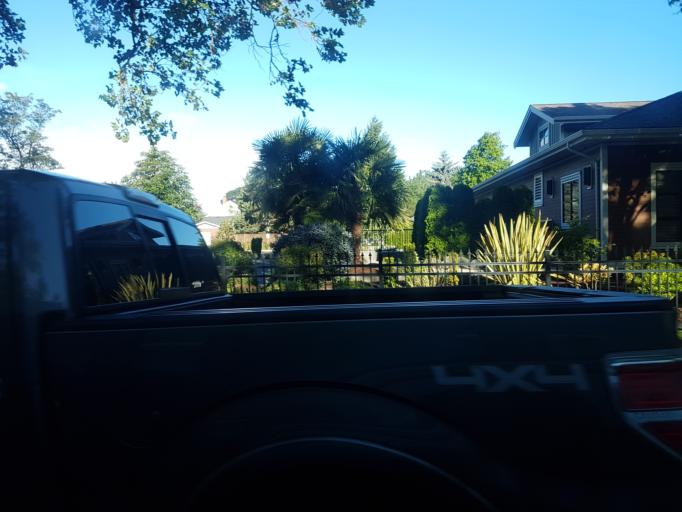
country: CA
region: British Columbia
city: Oak Bay
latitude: 48.4401
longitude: -123.3328
